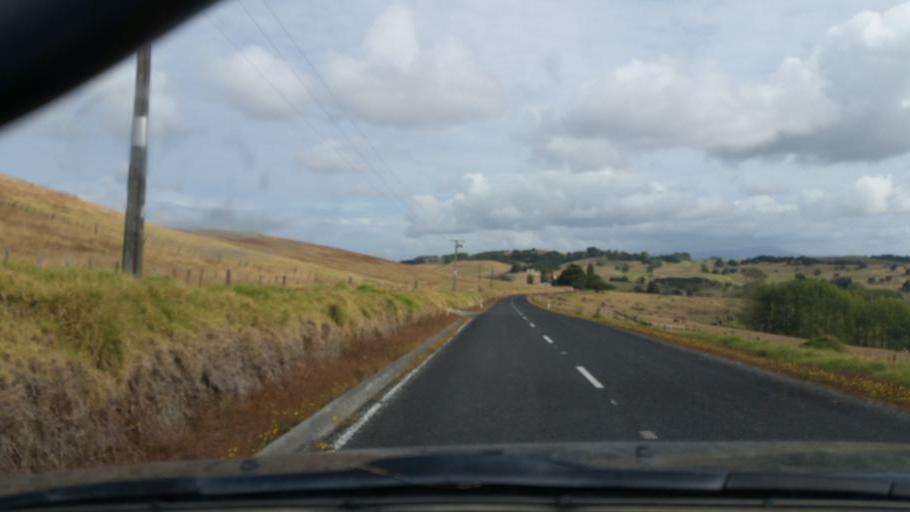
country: NZ
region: Northland
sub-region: Kaipara District
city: Dargaville
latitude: -35.9728
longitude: 173.9462
